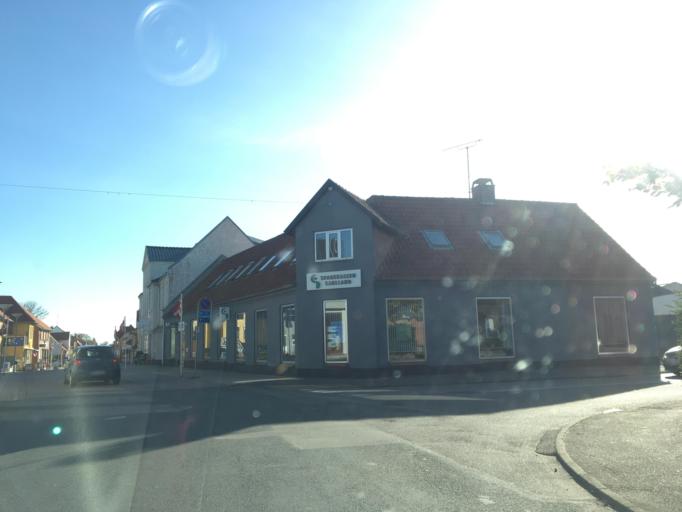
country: DK
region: Zealand
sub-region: Odsherred Kommune
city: Hojby
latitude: 55.8522
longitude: 11.5779
